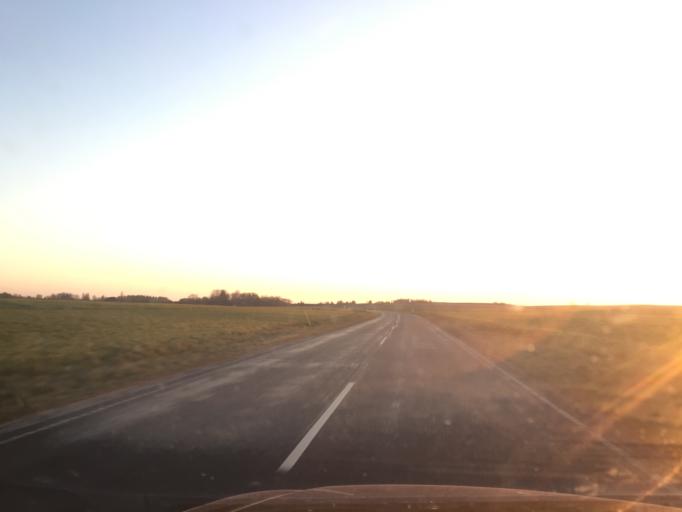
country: DK
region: Capital Region
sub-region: Allerod Kommune
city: Lynge
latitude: 55.8605
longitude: 12.2989
